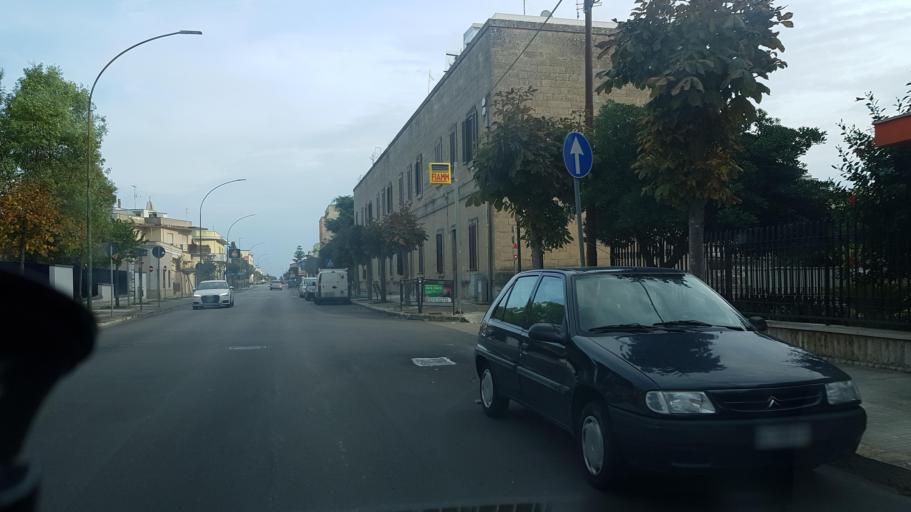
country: IT
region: Apulia
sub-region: Provincia di Lecce
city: Trepuzzi
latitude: 40.4019
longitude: 18.0771
